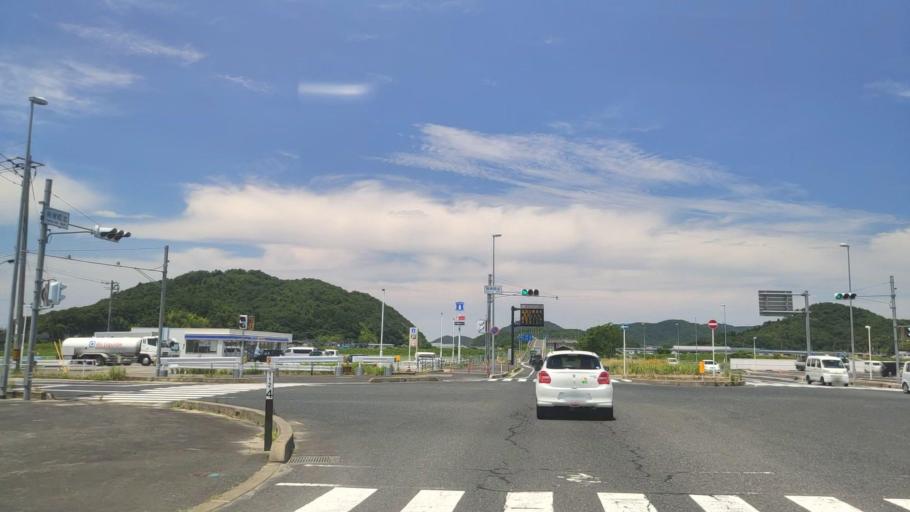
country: JP
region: Tottori
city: Tottori
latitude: 35.4617
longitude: 134.2430
